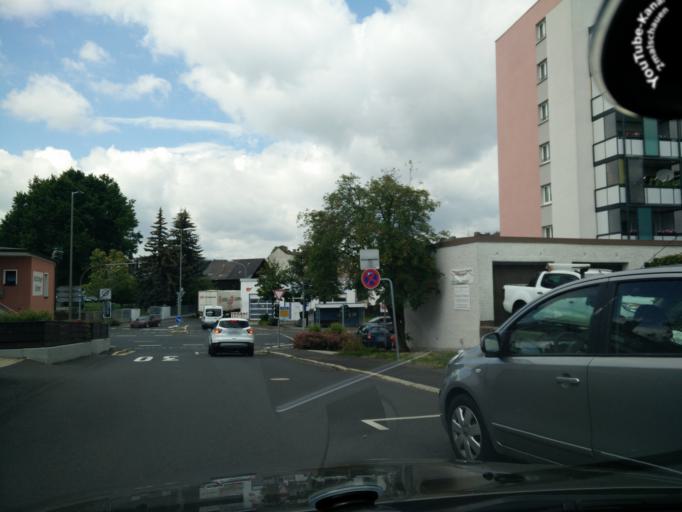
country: DE
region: Bavaria
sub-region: Upper Franconia
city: Marktredwitz
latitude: 49.9994
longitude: 12.0809
